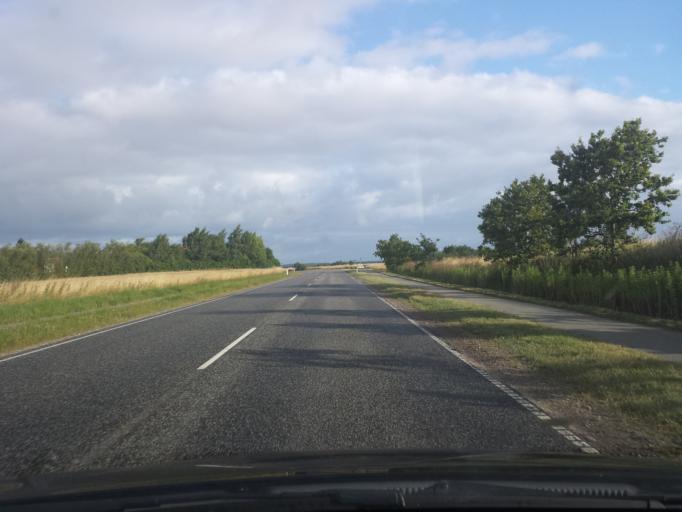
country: DK
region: South Denmark
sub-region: Sonderborg Kommune
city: Guderup
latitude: 55.0204
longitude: 9.8434
